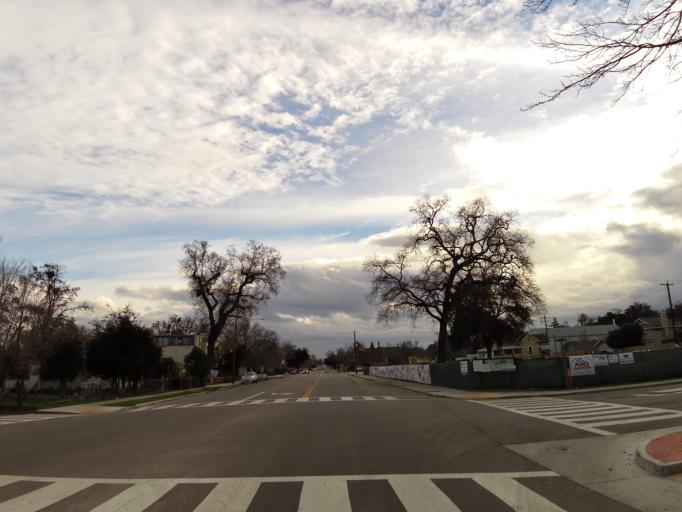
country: US
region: California
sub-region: San Luis Obispo County
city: Paso Robles
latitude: 35.6342
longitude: -120.6921
